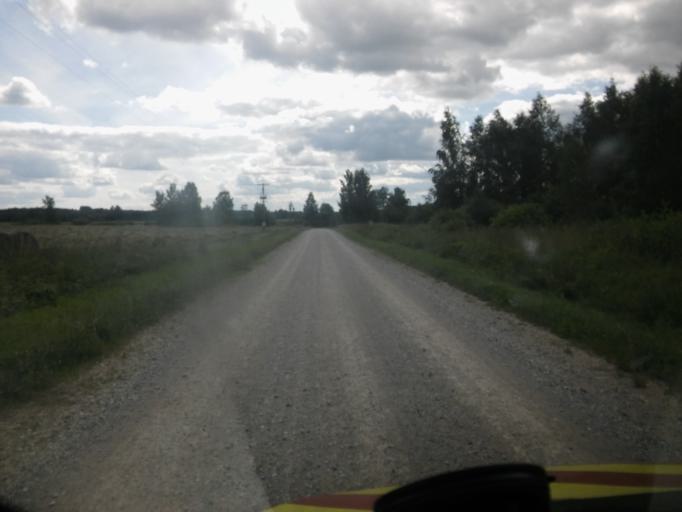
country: EE
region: Viljandimaa
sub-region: Karksi vald
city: Karksi-Nuia
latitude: 58.0991
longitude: 25.5007
